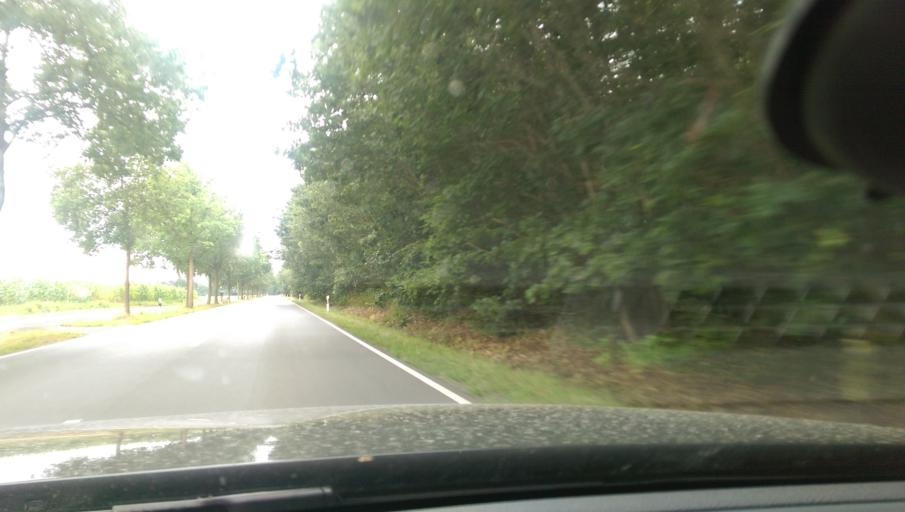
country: DE
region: Lower Saxony
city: Neustadt am Rubenberge
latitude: 52.5488
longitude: 9.4769
